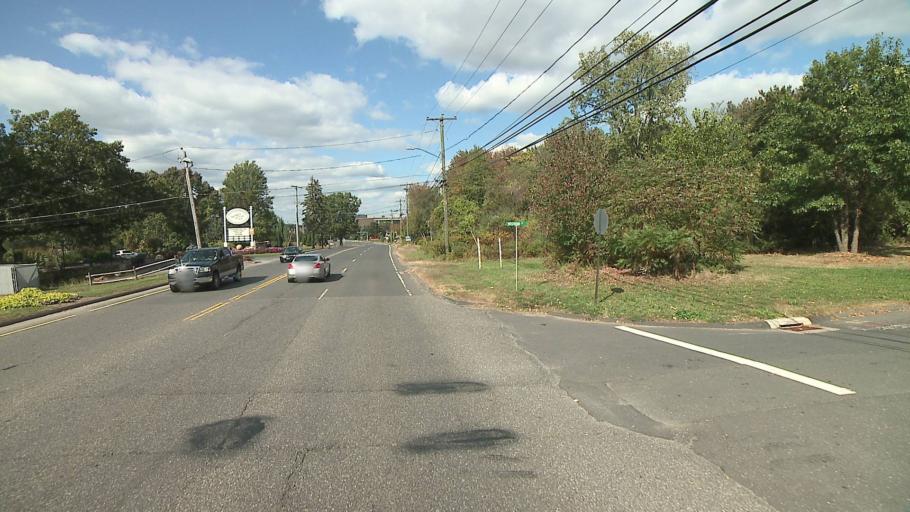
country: US
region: Connecticut
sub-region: Hartford County
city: Plainville
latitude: 41.6440
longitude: -72.9015
